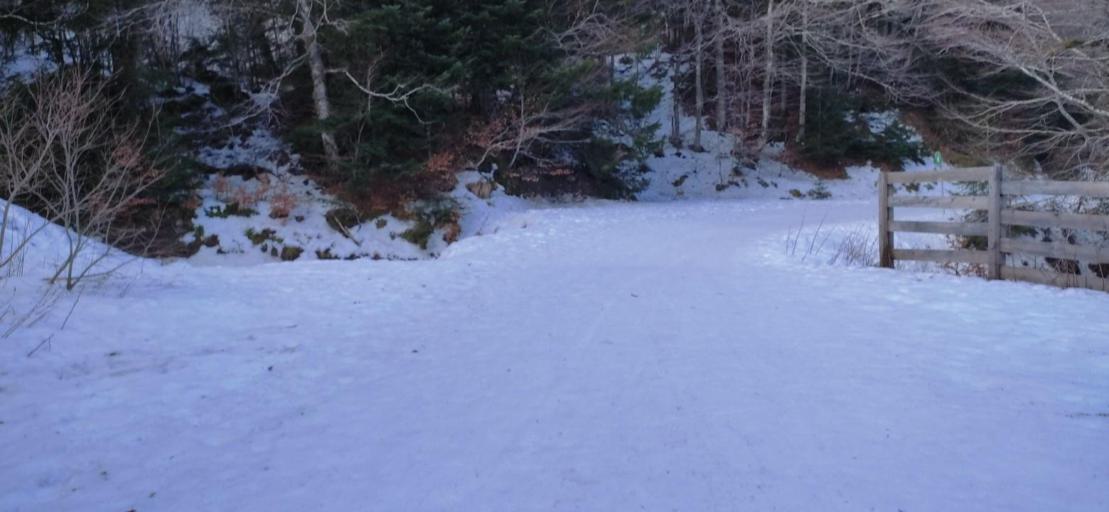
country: FR
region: Auvergne
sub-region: Departement du Puy-de-Dome
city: Mont-Dore
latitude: 45.5512
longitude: 2.8099
